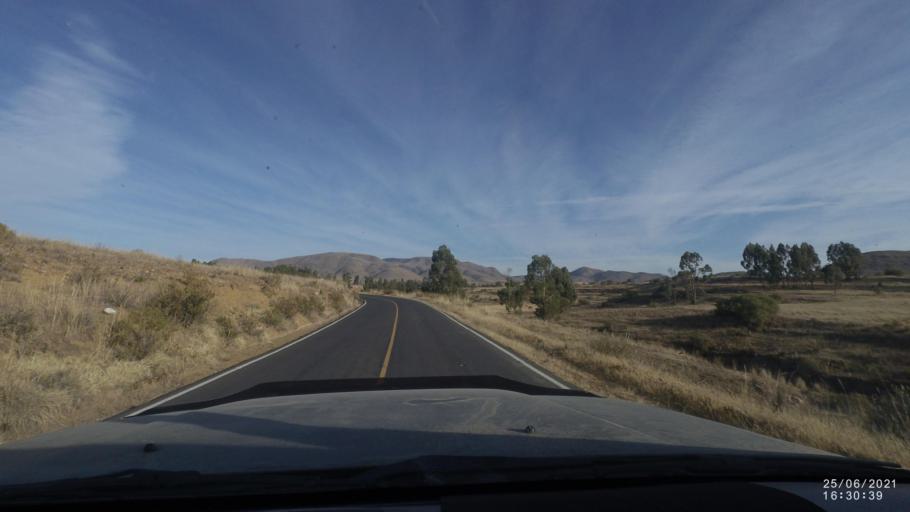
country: BO
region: Cochabamba
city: Arani
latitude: -17.7946
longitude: -65.8041
